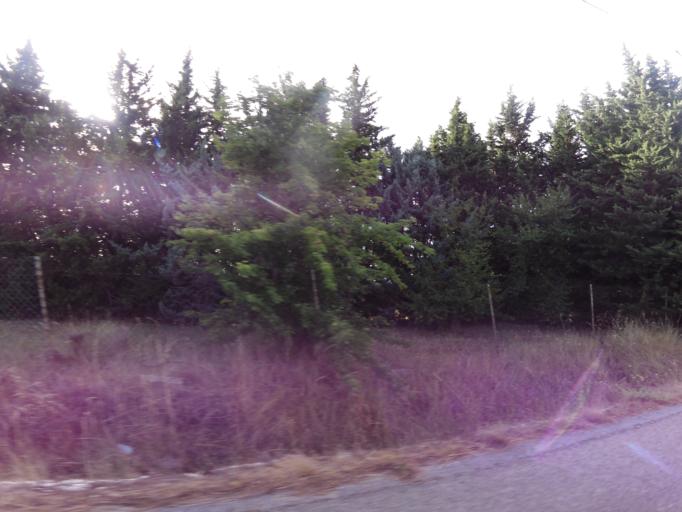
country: FR
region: Languedoc-Roussillon
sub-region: Departement du Gard
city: Saint-Mamert-du-Gard
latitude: 43.8514
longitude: 4.1515
